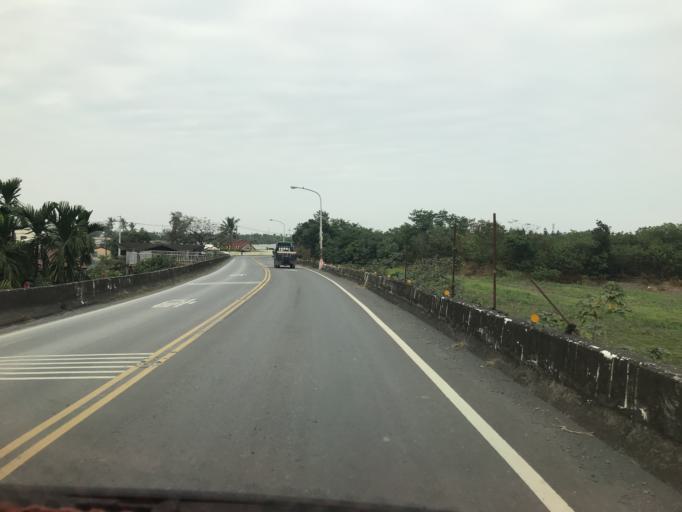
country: TW
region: Taiwan
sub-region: Pingtung
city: Pingtung
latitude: 22.4948
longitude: 120.5917
